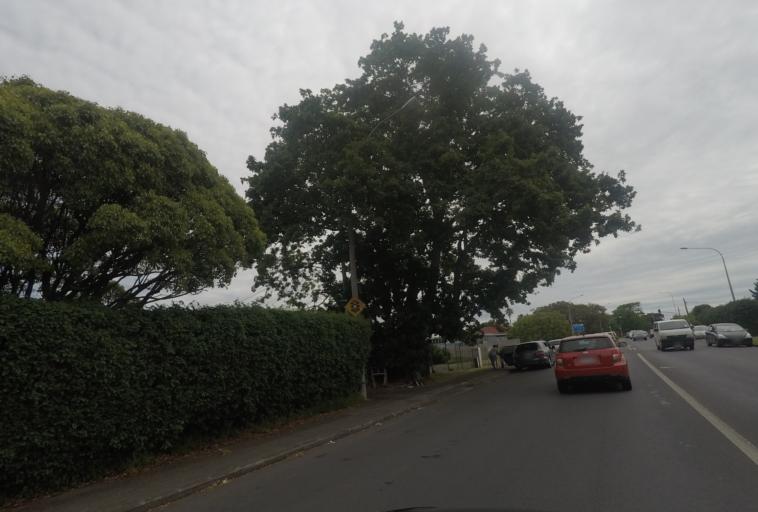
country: NZ
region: Auckland
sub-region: Auckland
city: Mangere
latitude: -36.9515
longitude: 174.8421
